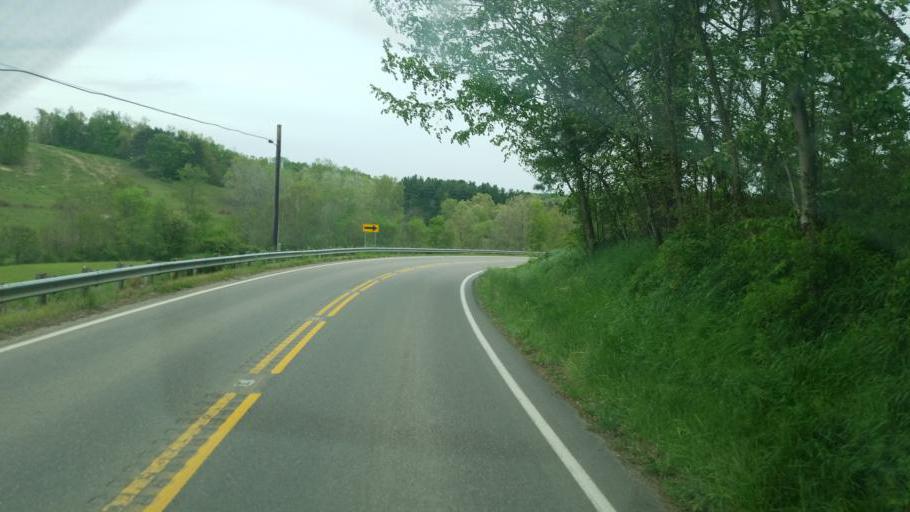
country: US
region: Ohio
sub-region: Tuscarawas County
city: Newcomerstown
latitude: 40.2156
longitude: -81.5095
